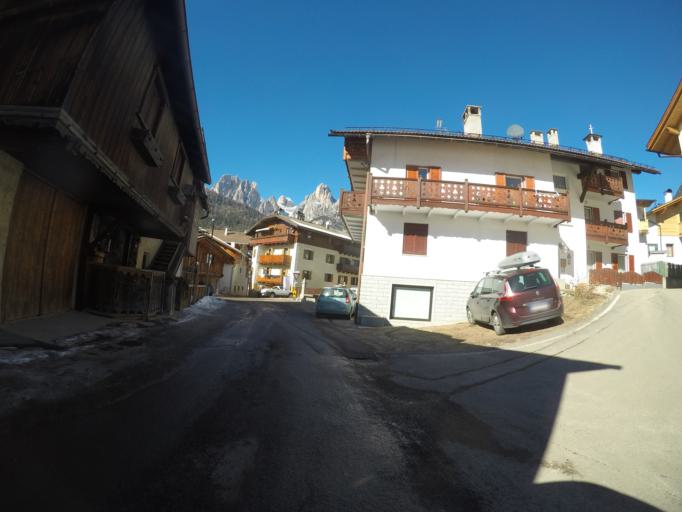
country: IT
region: Trentino-Alto Adige
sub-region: Provincia di Trento
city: Pozza di Fassa
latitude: 46.4301
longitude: 11.6951
